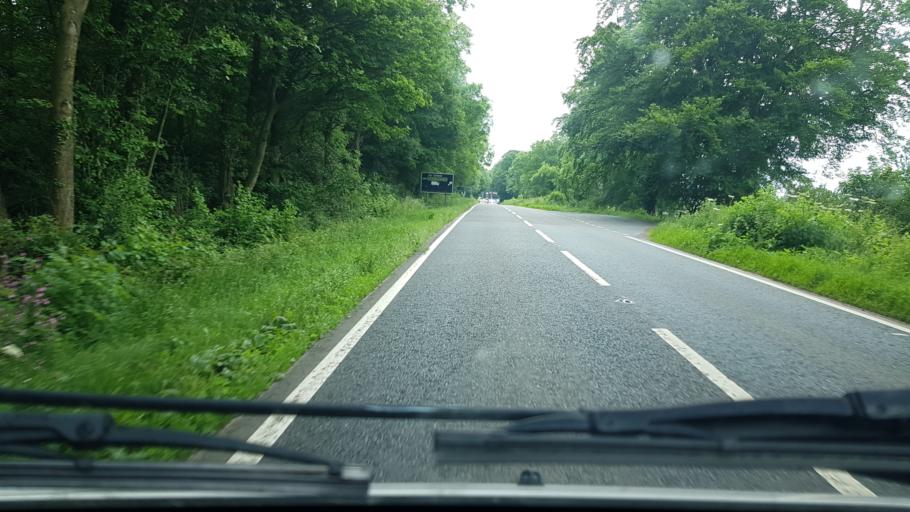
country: GB
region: England
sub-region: Gloucestershire
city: Chipping Campden
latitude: 52.0009
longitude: -1.7855
